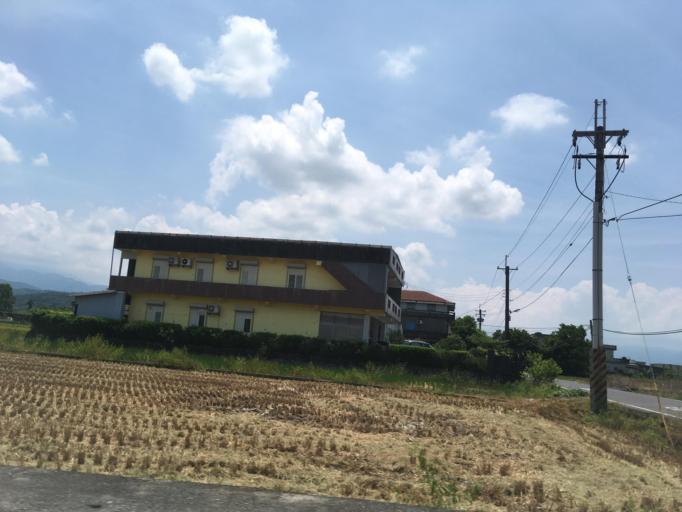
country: TW
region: Taiwan
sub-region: Yilan
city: Yilan
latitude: 24.6462
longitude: 121.7642
